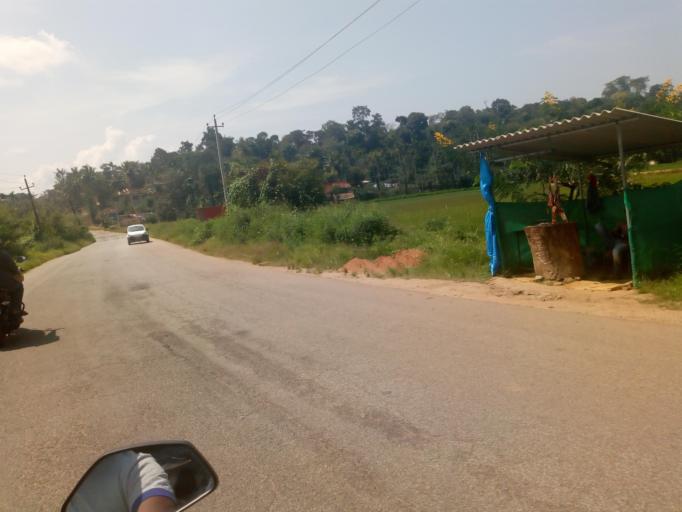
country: IN
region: Karnataka
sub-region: Kodagu
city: Ponnampet
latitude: 12.1252
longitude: 75.9416
